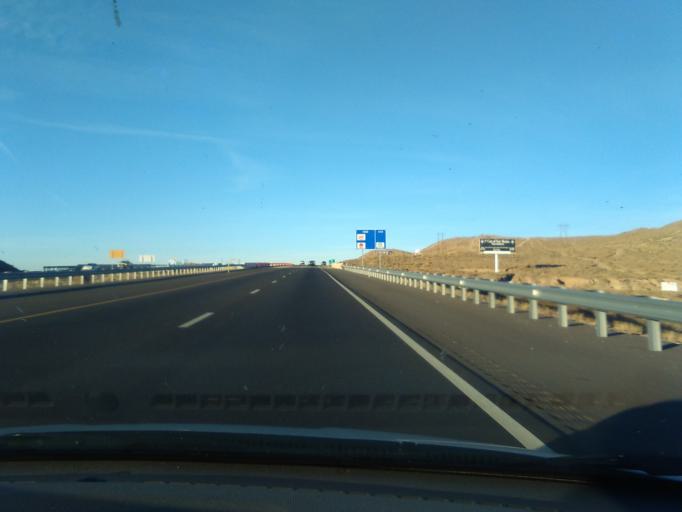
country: US
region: New Mexico
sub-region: Bernalillo County
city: South Valley
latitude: 35.0085
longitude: -106.6422
